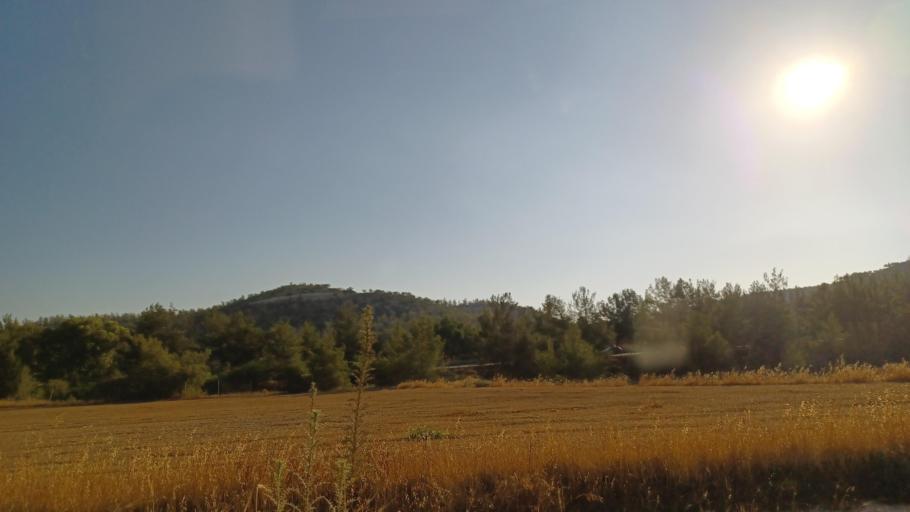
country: CY
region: Lefkosia
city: Lympia
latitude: 34.9819
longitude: 33.5133
